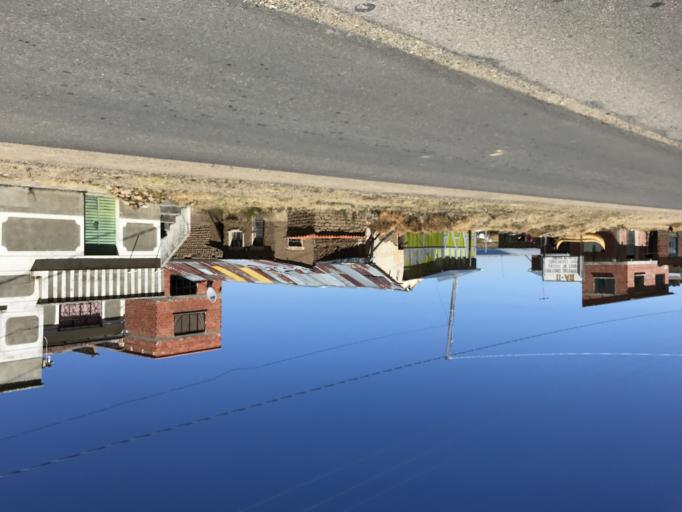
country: BO
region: La Paz
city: Huatajata
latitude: -16.2148
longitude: -68.6784
